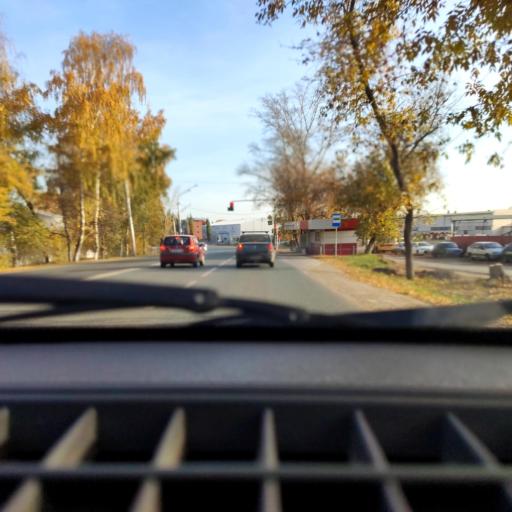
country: RU
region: Bashkortostan
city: Avdon
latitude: 54.6841
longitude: 55.8126
